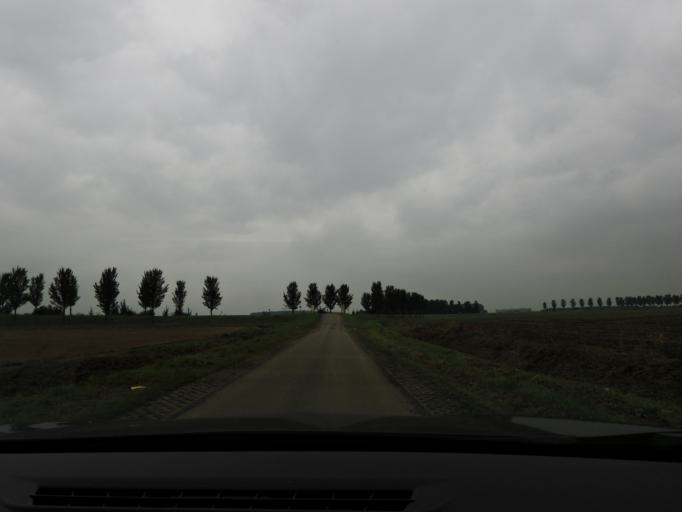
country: NL
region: South Holland
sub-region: Gemeente Goeree-Overflakkee
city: Middelharnis
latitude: 51.7497
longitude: 4.1955
